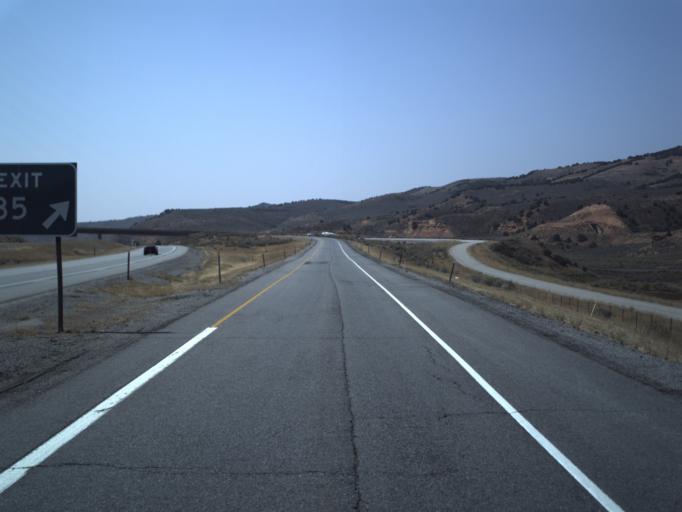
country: US
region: Wyoming
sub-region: Uinta County
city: Evanston
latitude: 41.1219
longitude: -111.1868
